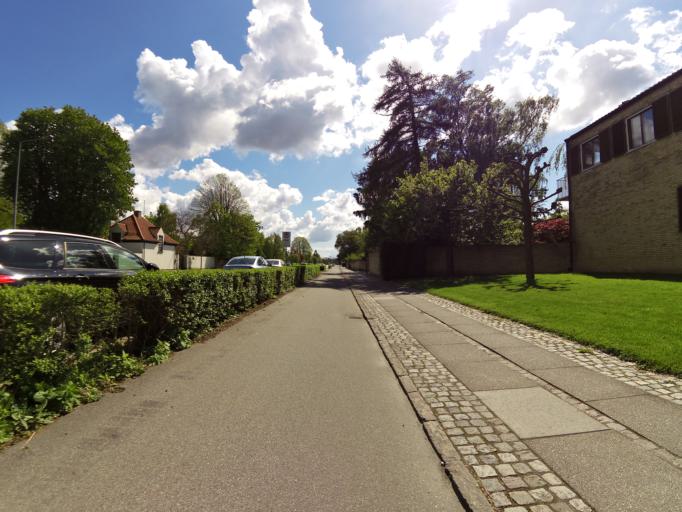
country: DK
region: Capital Region
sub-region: Gentofte Kommune
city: Charlottenlund
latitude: 55.7291
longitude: 12.5550
